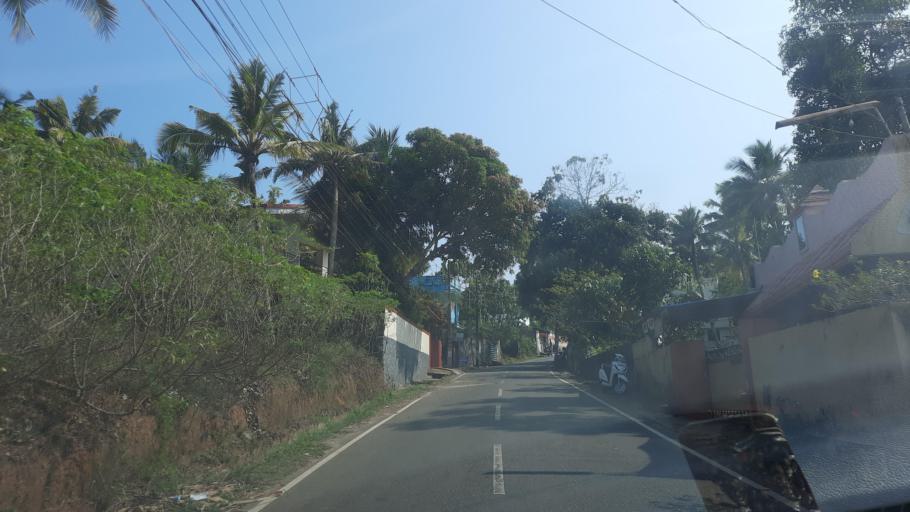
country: IN
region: Kerala
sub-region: Thiruvananthapuram
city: Nedumangad
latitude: 8.5804
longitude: 76.9285
